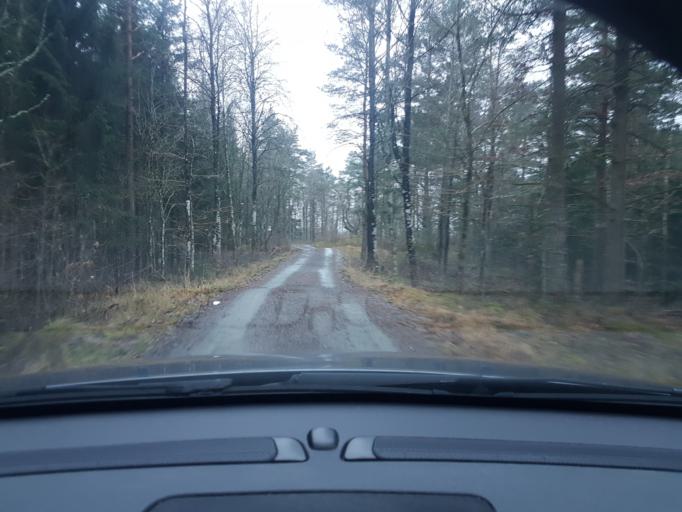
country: SE
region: Vaestra Goetaland
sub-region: Ale Kommun
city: Alvangen
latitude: 57.9562
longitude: 12.1378
